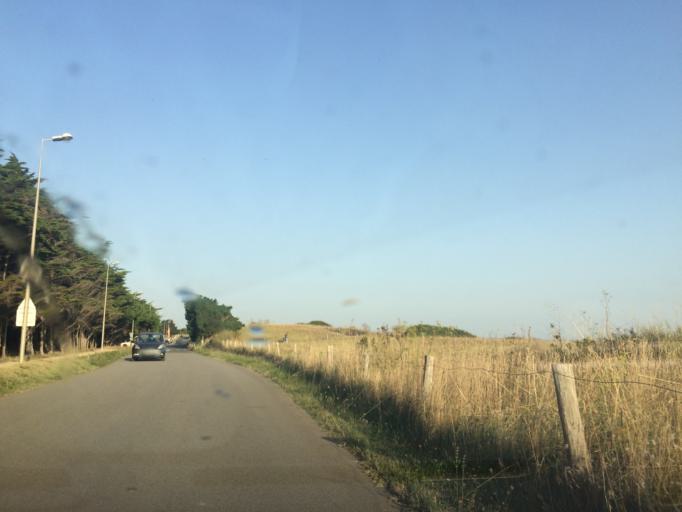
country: FR
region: Brittany
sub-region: Departement du Morbihan
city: Damgan
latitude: 47.5163
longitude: -2.5673
